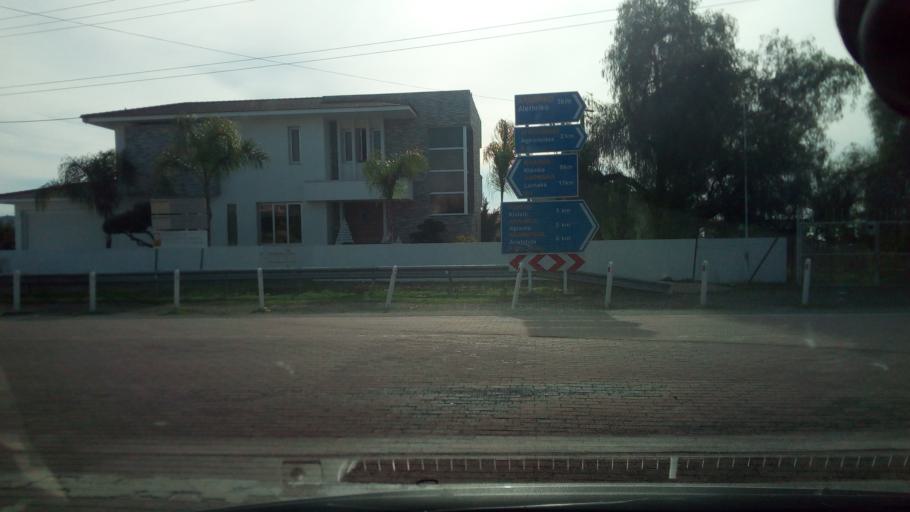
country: CY
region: Larnaka
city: Tersefanou
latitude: 34.8666
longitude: 33.4965
